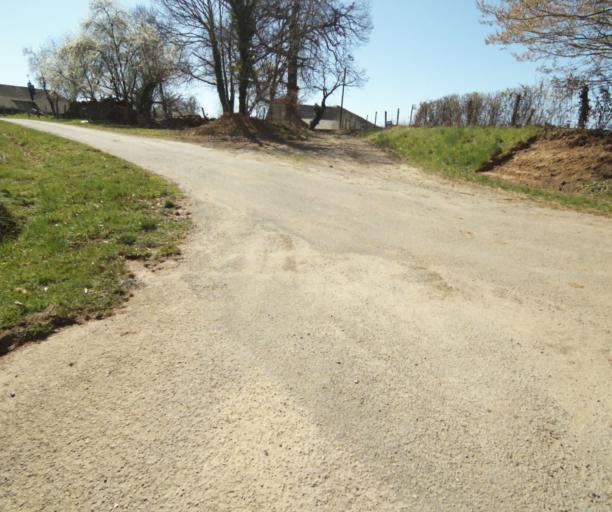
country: FR
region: Limousin
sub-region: Departement de la Correze
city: Uzerche
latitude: 45.4019
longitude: 1.6278
